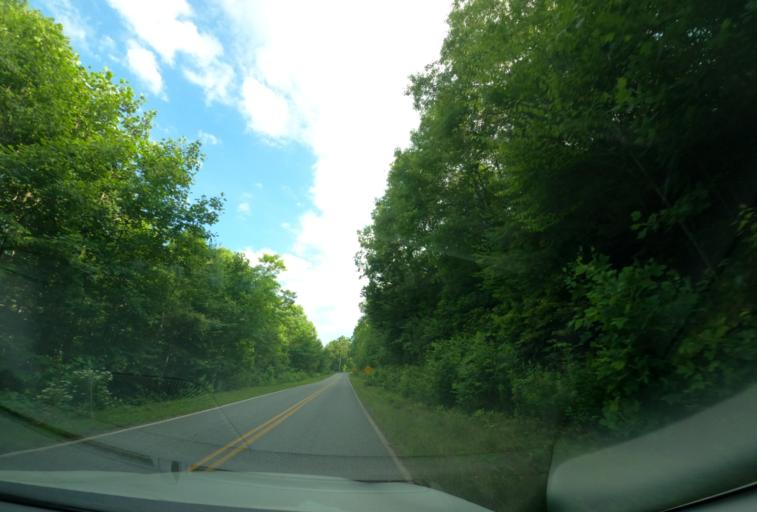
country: US
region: North Carolina
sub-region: Transylvania County
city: Brevard
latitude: 35.2326
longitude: -82.8581
